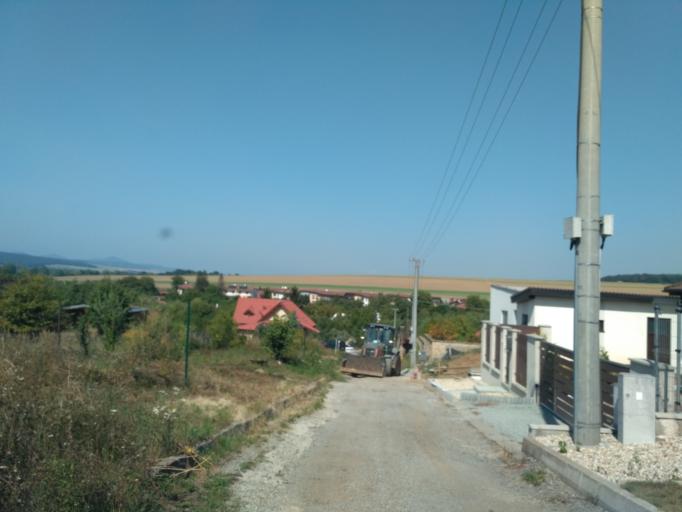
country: SK
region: Kosicky
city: Kosice
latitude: 48.7563
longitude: 21.3458
